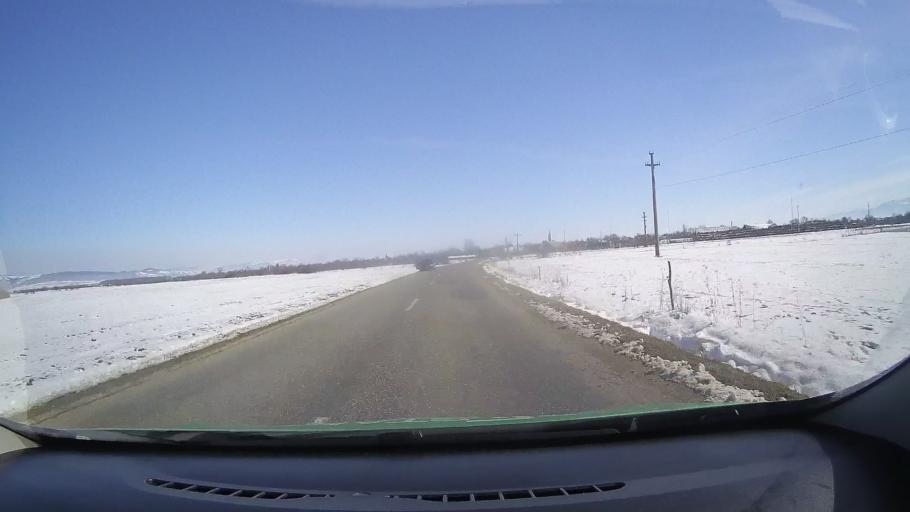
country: RO
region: Brasov
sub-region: Comuna Dragus
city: Dragus
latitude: 45.7586
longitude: 24.7652
